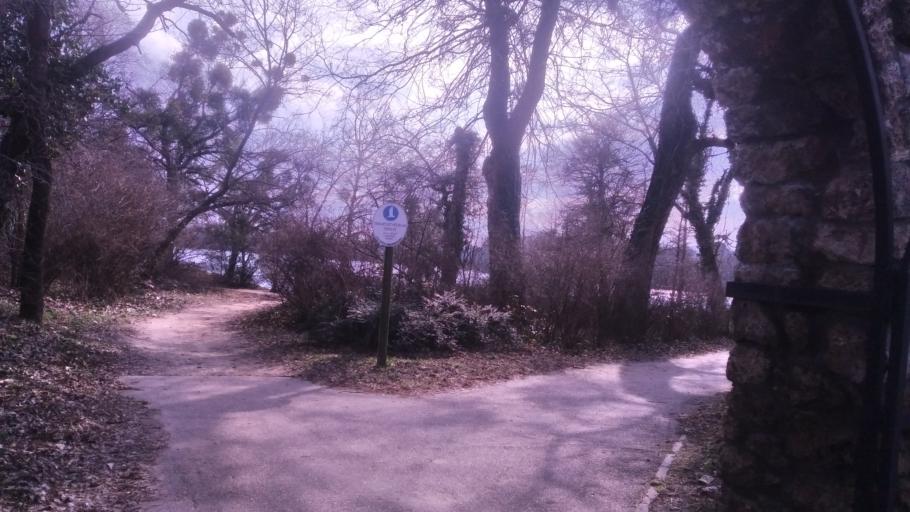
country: HU
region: Komarom-Esztergom
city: Tata
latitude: 47.6535
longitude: 18.3328
